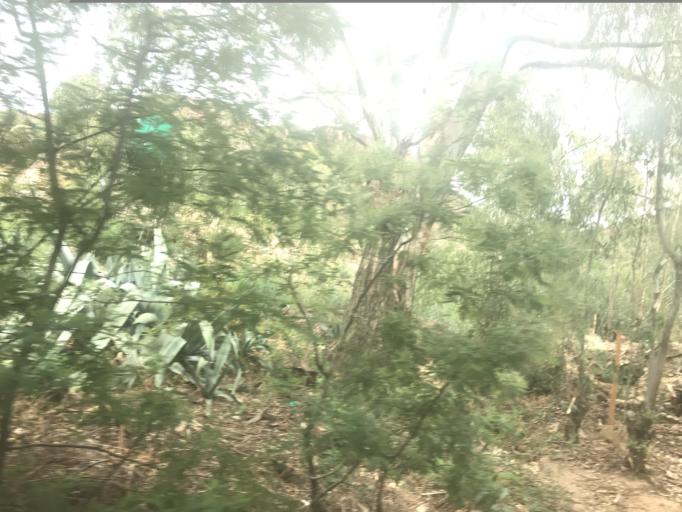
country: LS
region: Maseru
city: Nako
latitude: -29.6320
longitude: 27.5139
